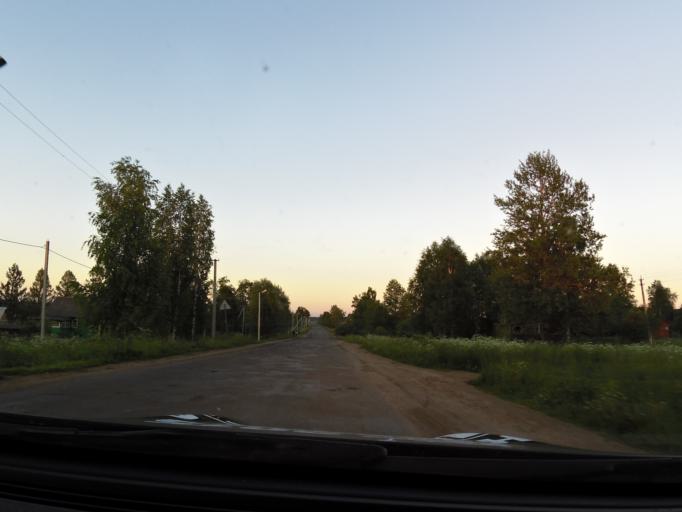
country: RU
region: Leningrad
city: Voznesen'ye
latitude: 60.8505
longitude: 35.5589
